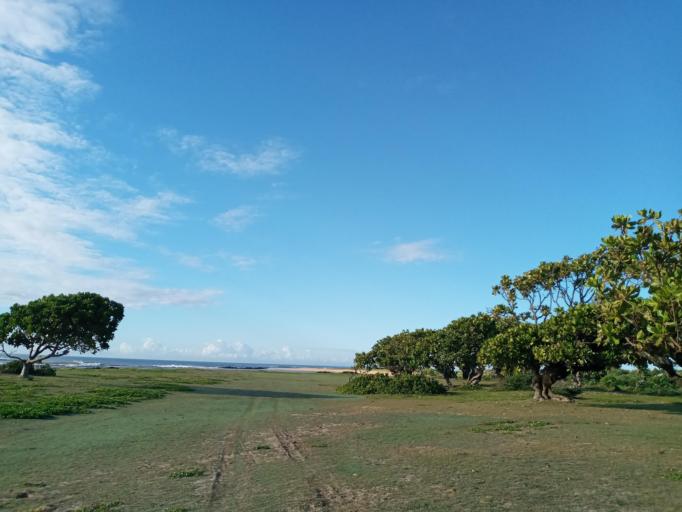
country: MG
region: Atsimo-Atsinanana
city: Vohipaho
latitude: -23.5582
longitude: 47.6277
